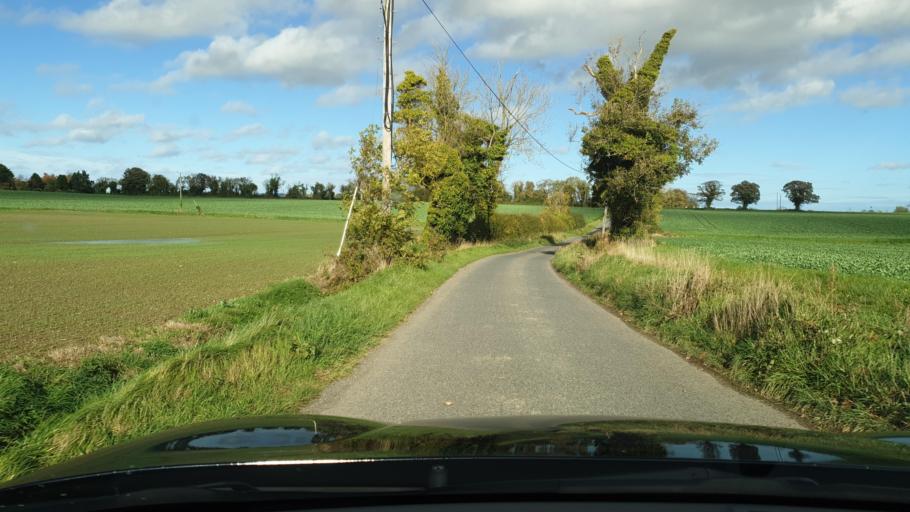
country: IE
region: Leinster
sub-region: Fingal County
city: Swords
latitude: 53.5004
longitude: -6.2420
